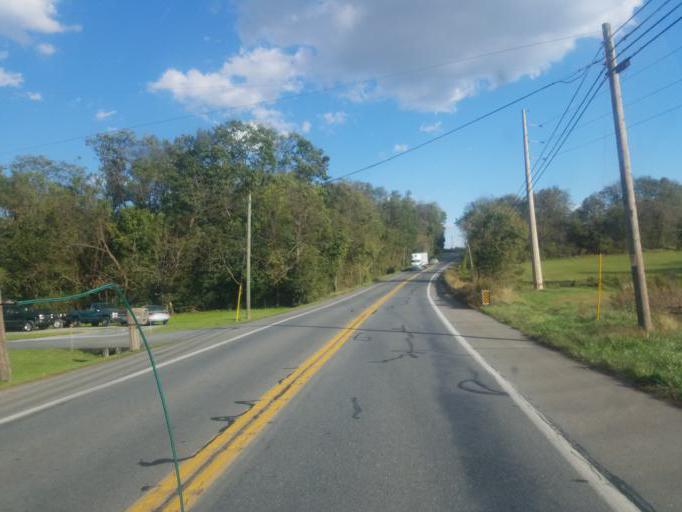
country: US
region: Pennsylvania
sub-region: Lancaster County
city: Bainbridge
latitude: 40.0772
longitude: -76.6470
